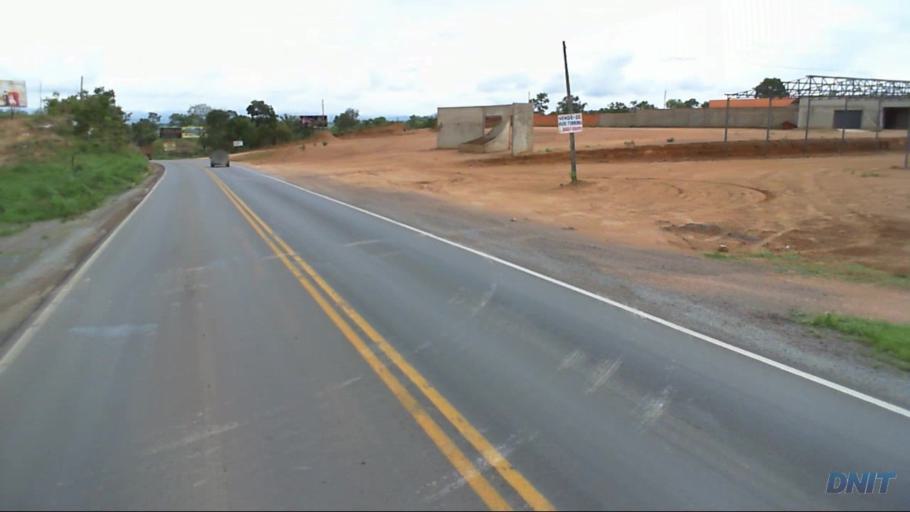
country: BR
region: Goias
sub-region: Padre Bernardo
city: Padre Bernardo
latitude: -15.1825
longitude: -48.2846
